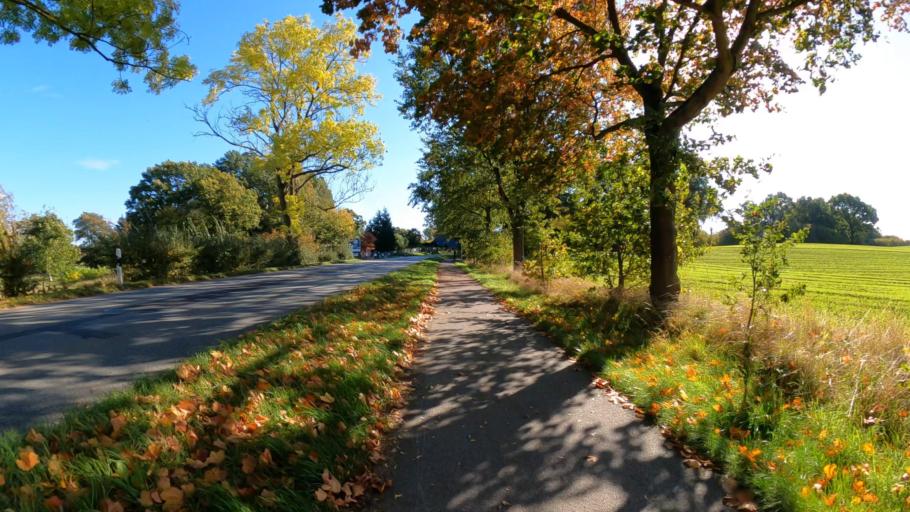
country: DE
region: Schleswig-Holstein
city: Ahrensburg
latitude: 53.6911
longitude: 10.2229
